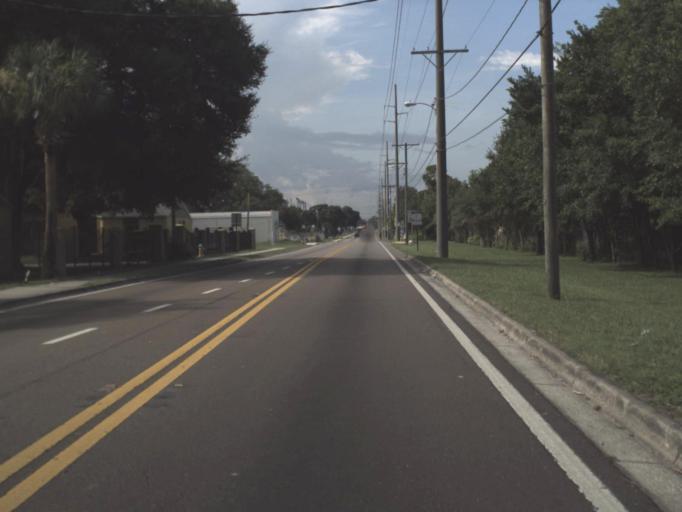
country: US
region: Florida
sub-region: Hillsborough County
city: Tampa
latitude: 27.9877
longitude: -82.4348
